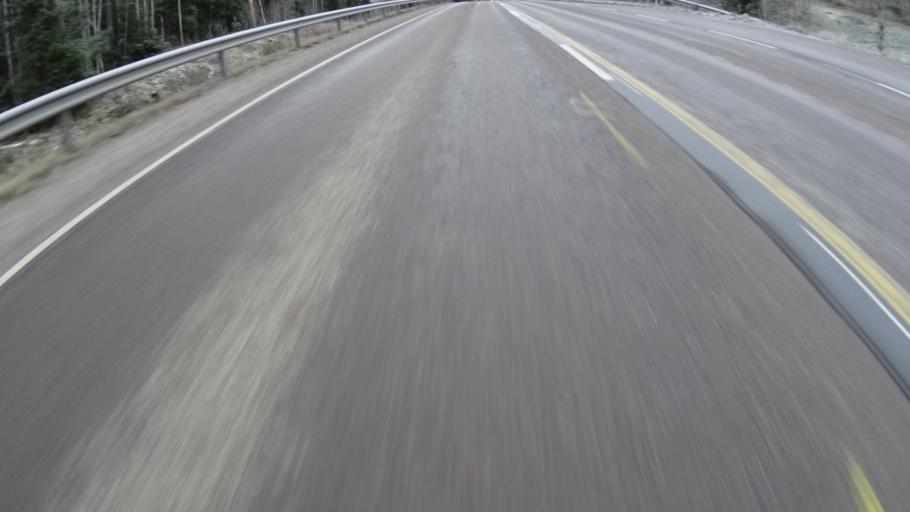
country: FI
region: Uusimaa
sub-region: Helsinki
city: Nurmijaervi
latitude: 60.4074
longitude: 24.7312
